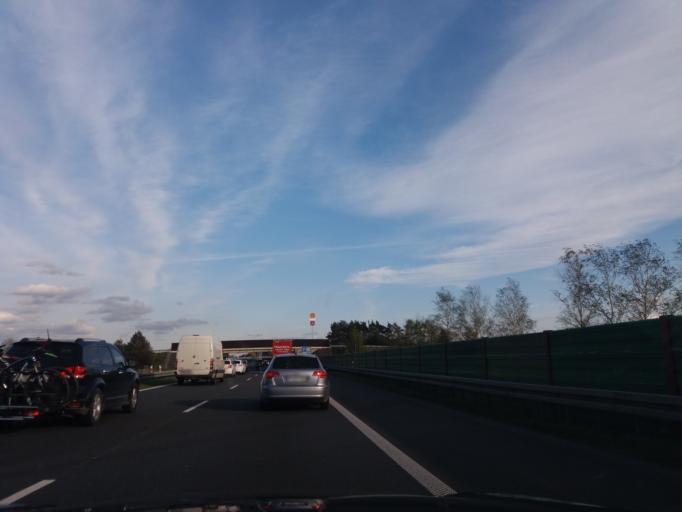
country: PL
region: Opole Voivodeship
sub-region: Powiat opolski
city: Niemodlin
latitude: 50.6805
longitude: 17.6470
